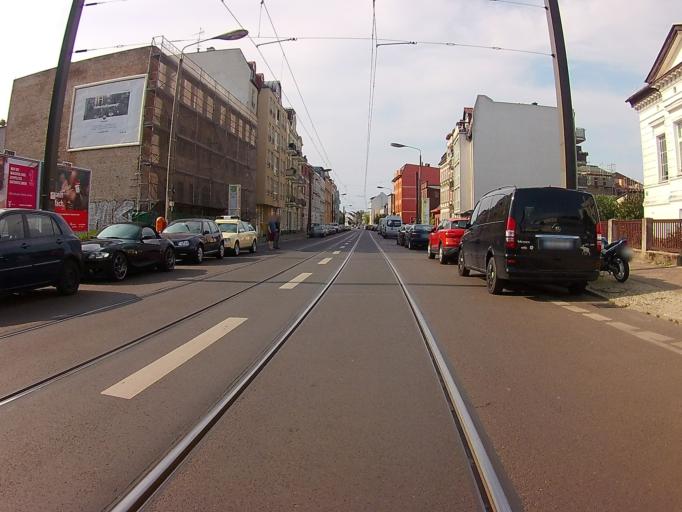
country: DE
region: Berlin
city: Kopenick Bezirk
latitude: 52.4385
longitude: 13.5716
